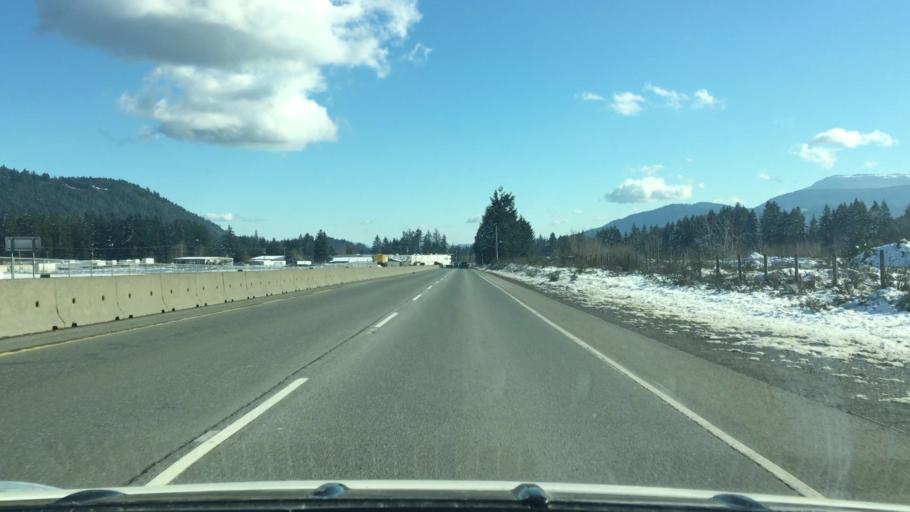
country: CA
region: British Columbia
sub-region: Cowichan Valley Regional District
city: Ladysmith
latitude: 49.0427
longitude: -123.8702
